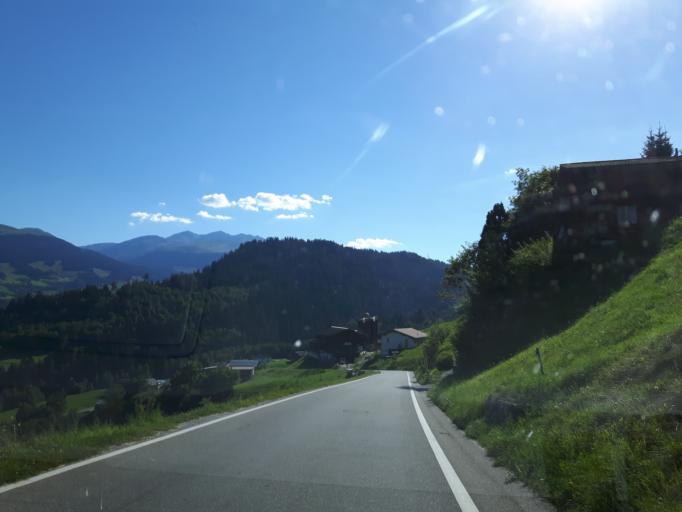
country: CH
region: Grisons
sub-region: Surselva District
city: Breil
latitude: 46.7811
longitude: 9.1078
